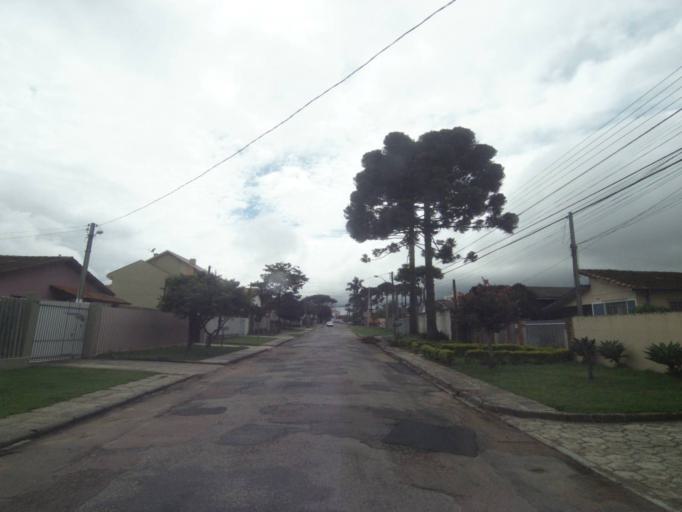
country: BR
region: Parana
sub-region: Curitiba
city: Curitiba
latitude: -25.4863
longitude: -49.3006
